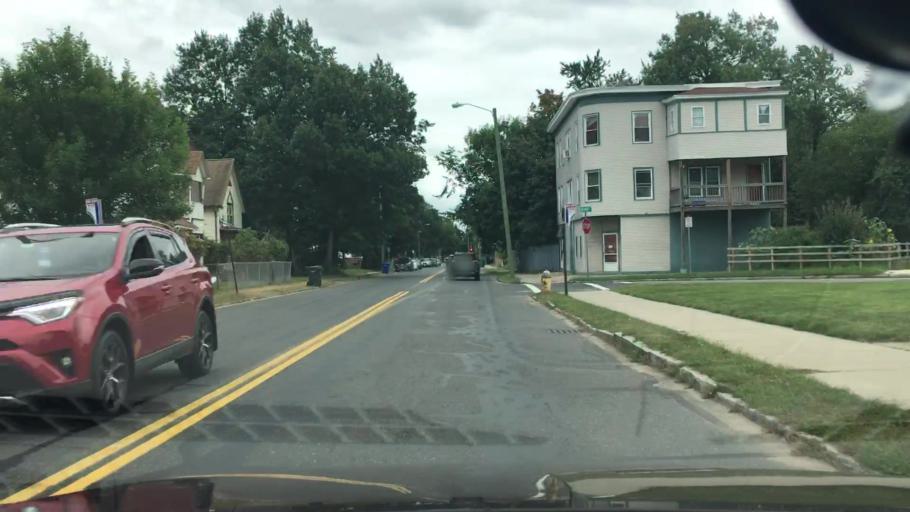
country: US
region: Massachusetts
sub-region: Hampden County
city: Springfield
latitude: 42.0947
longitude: -72.5591
